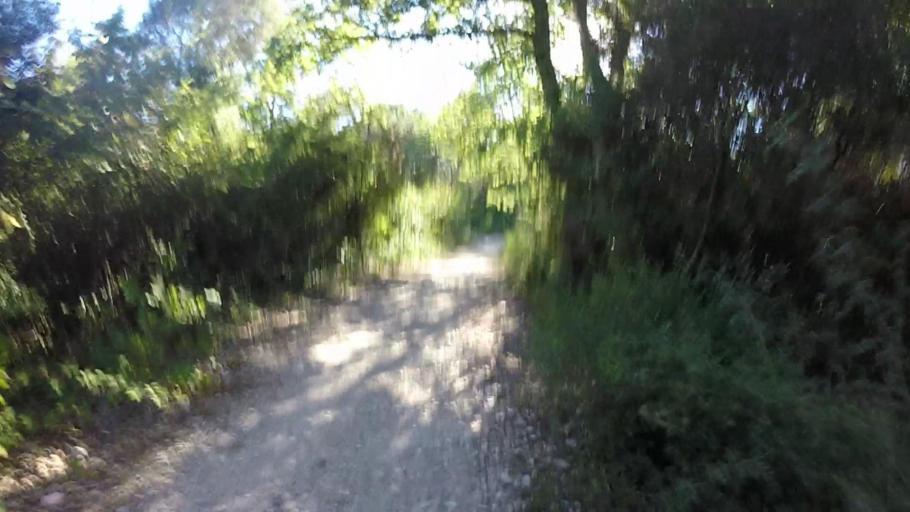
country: FR
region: Provence-Alpes-Cote d'Azur
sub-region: Departement des Alpes-Maritimes
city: Mougins
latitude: 43.6163
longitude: 7.0389
